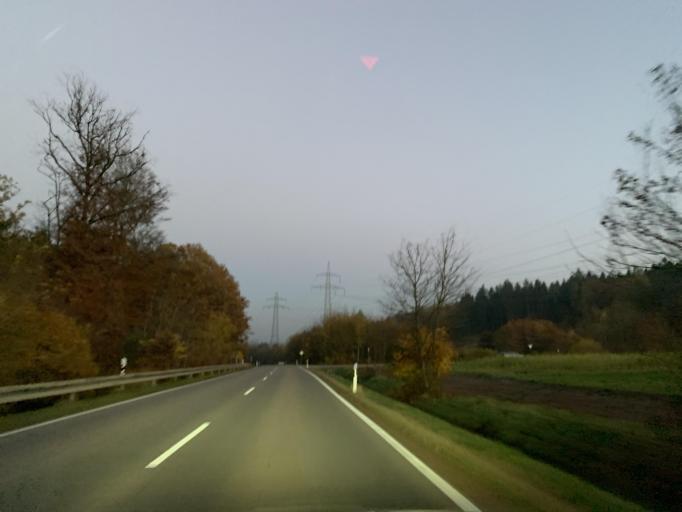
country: DE
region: Bavaria
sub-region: Upper Palatinate
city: Brunn
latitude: 49.2407
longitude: 12.2177
